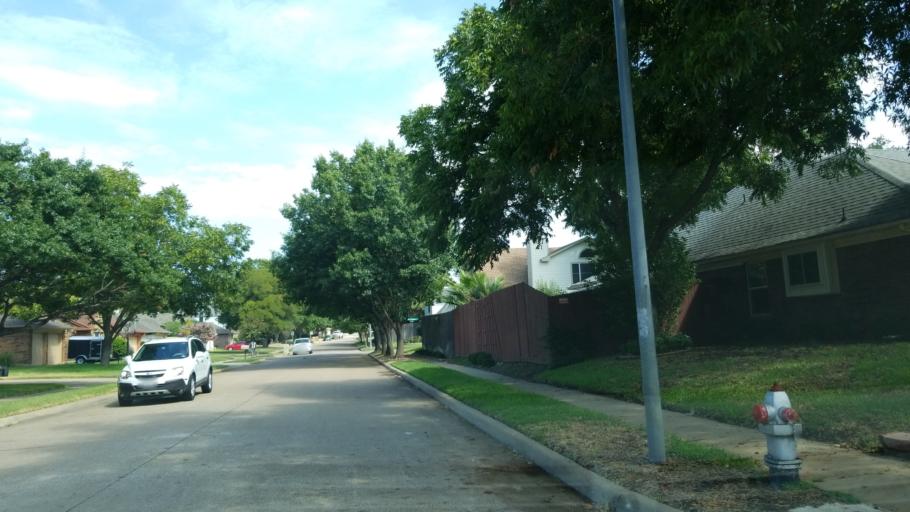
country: US
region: Texas
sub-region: Tarrant County
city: Euless
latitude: 32.8840
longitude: -97.0948
